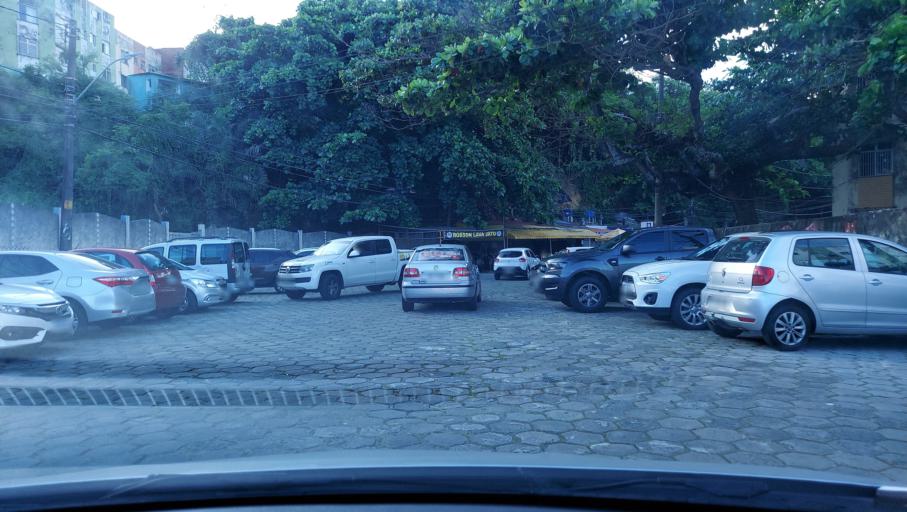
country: BR
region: Bahia
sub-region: Salvador
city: Salvador
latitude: -12.9798
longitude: -38.4451
